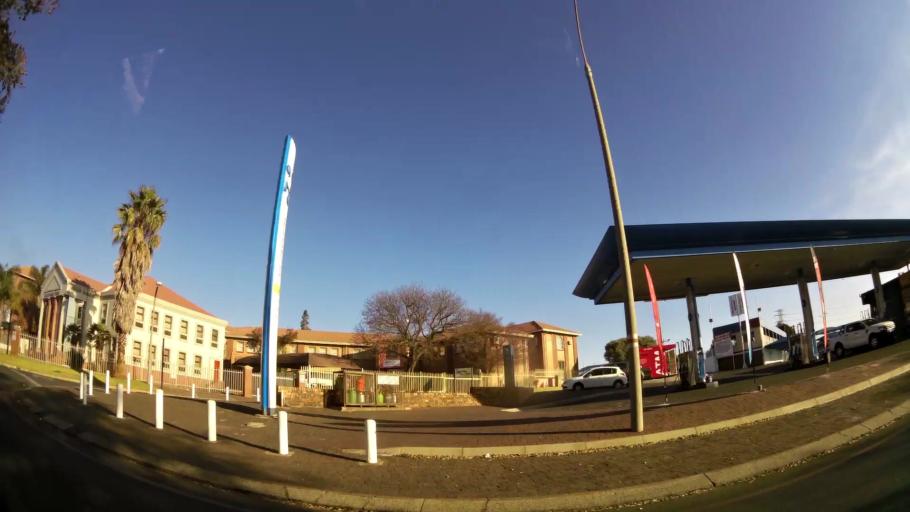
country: ZA
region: Gauteng
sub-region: City of Johannesburg Metropolitan Municipality
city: Roodepoort
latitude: -26.1386
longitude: 27.8674
